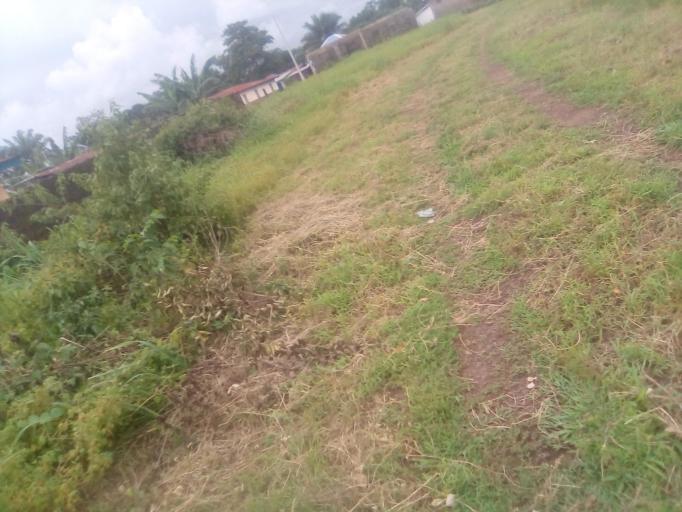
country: SL
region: Southern Province
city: Moyamba
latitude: 8.1485
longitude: -12.4330
